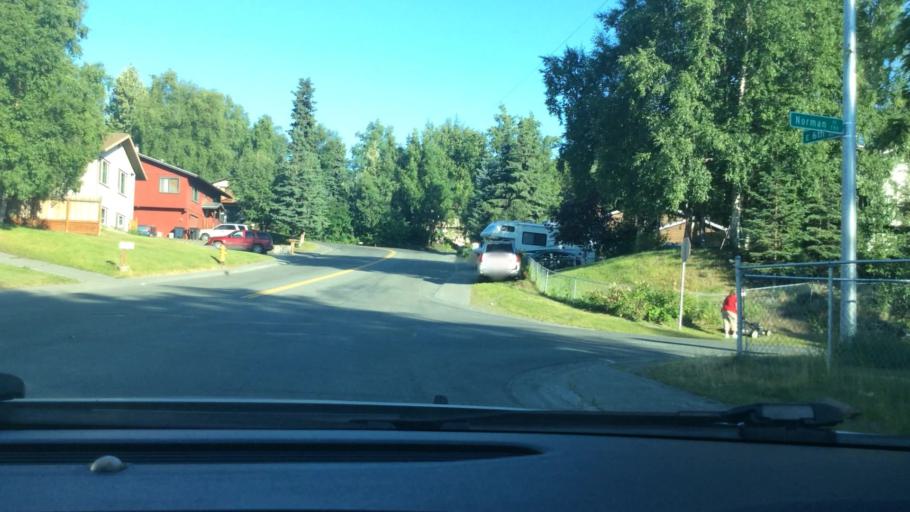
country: US
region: Alaska
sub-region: Anchorage Municipality
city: Anchorage
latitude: 61.2168
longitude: -149.7683
